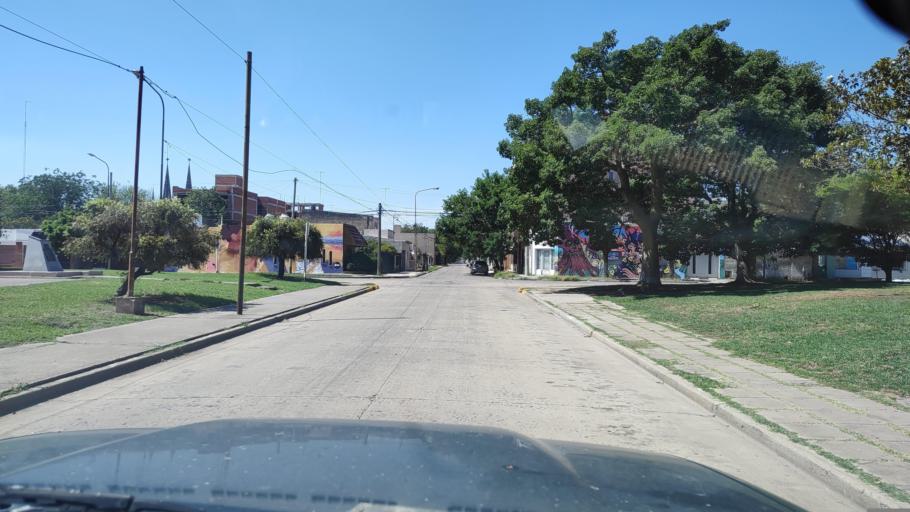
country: AR
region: Buenos Aires
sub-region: Partido de Lujan
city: Lujan
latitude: -34.5709
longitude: -59.1205
